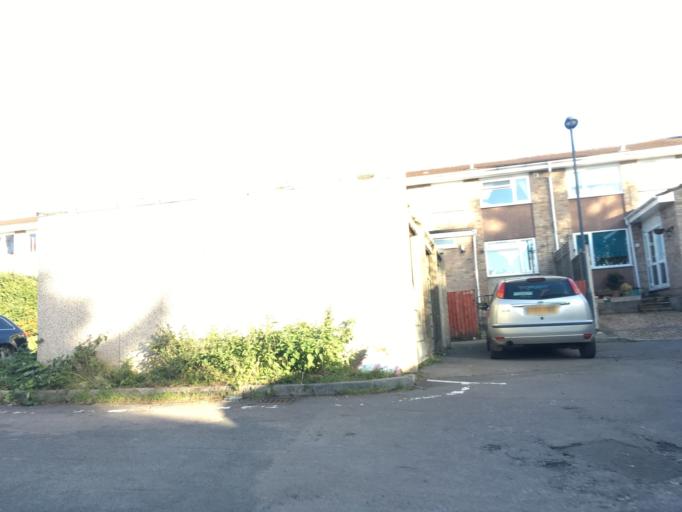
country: GB
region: England
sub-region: South Gloucestershire
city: Thornbury
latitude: 51.6115
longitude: -2.5173
